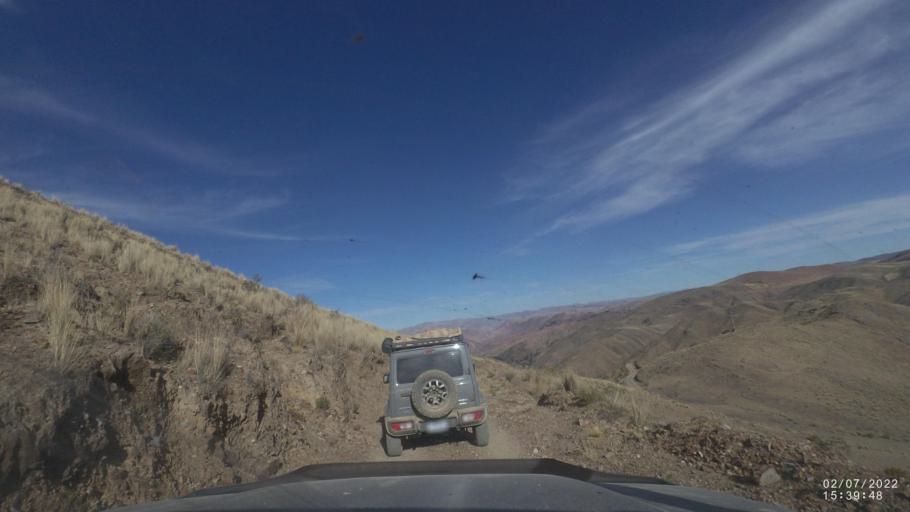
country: BO
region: Cochabamba
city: Irpa Irpa
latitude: -17.8978
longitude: -66.4107
